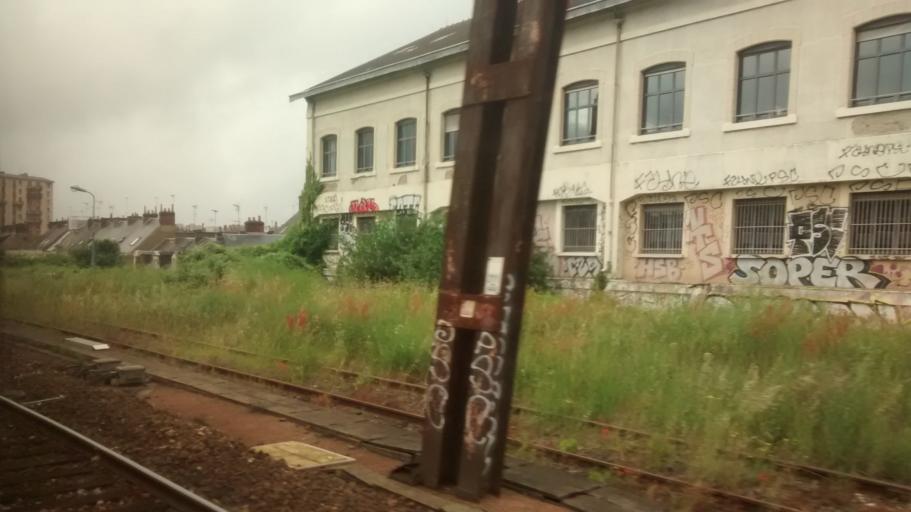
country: FR
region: Pays de la Loire
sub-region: Departement de la Sarthe
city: Le Mans
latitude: 47.9983
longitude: 0.1847
